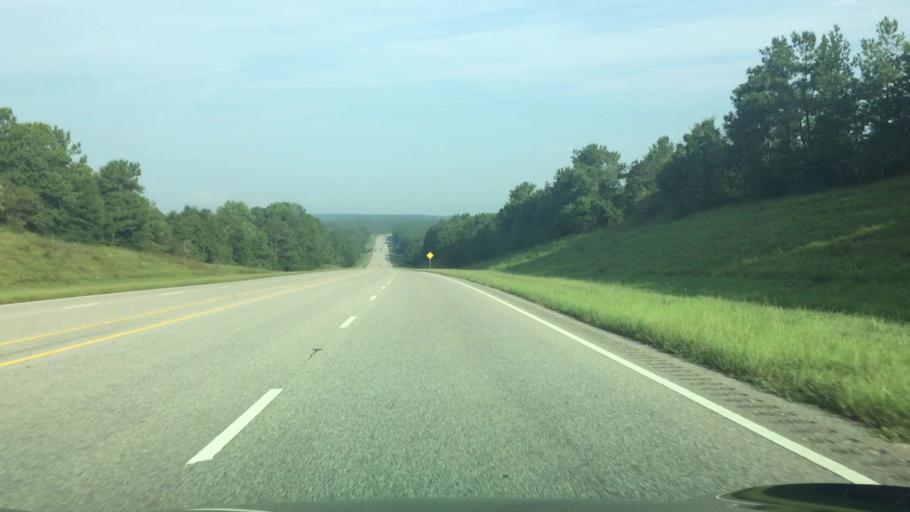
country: US
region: Alabama
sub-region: Butler County
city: Georgiana
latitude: 31.4621
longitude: -86.6463
